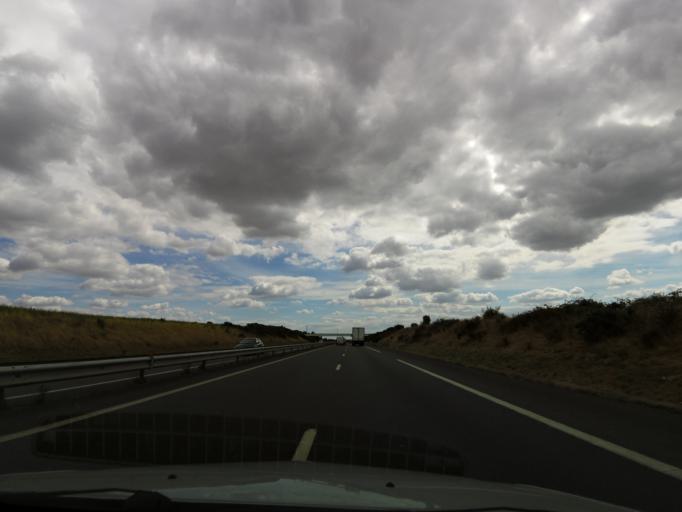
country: FR
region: Pays de la Loire
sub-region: Departement de la Loire-Atlantique
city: La Planche
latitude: 47.0412
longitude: -1.4104
